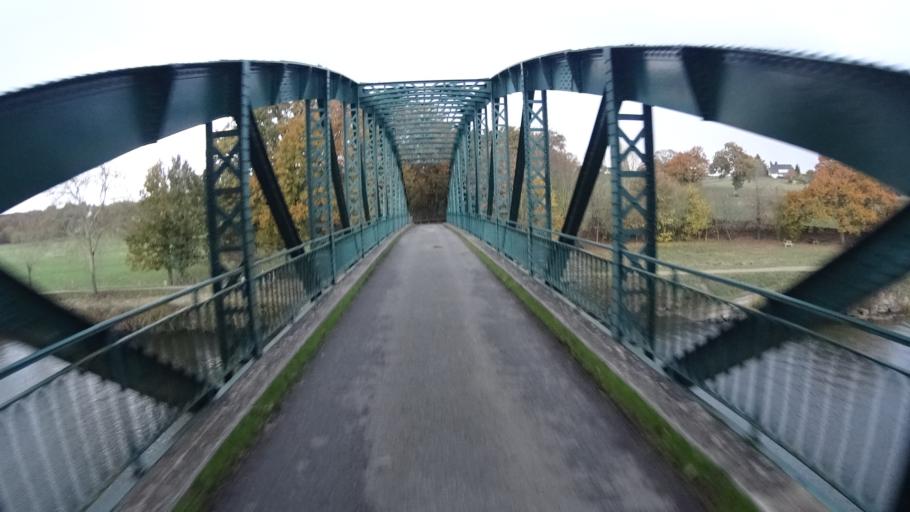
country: FR
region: Pays de la Loire
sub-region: Departement de la Loire-Atlantique
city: Saint-Nicolas-de-Redon
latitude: 47.6720
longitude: -2.0352
